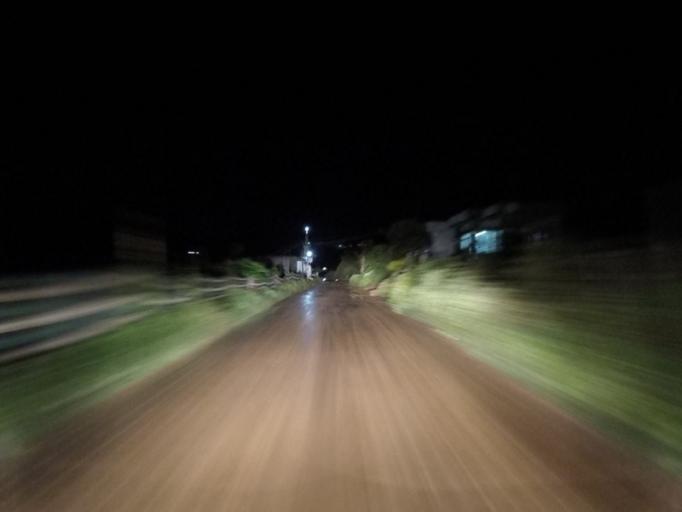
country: IN
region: Tamil Nadu
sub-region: Nilgiri
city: Kotagiri
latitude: 11.4821
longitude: 76.8225
